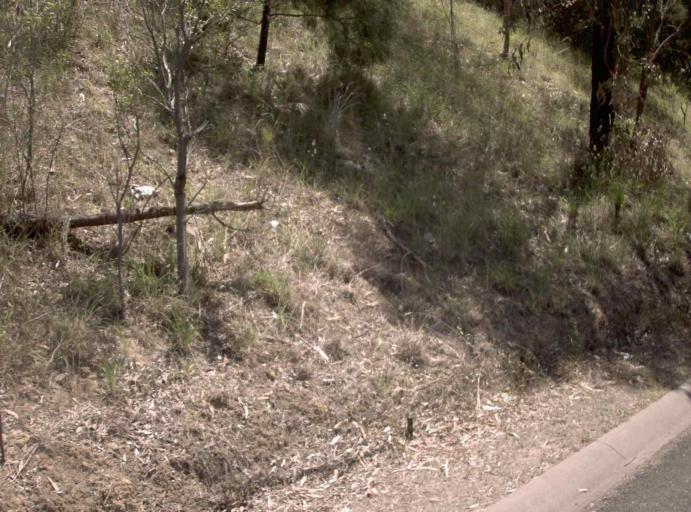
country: AU
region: Victoria
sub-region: East Gippsland
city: Lakes Entrance
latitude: -37.8515
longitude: 148.0377
